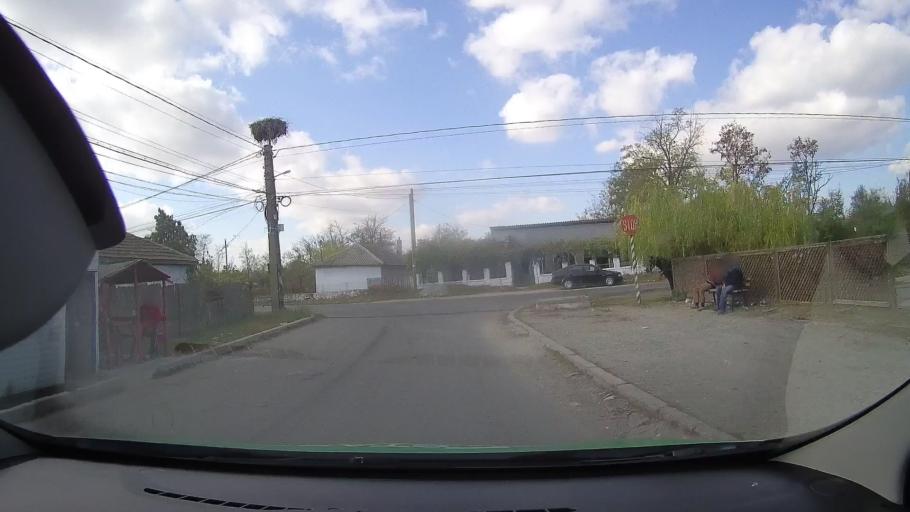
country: RO
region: Constanta
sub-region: Comuna Istria
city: Istria
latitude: 44.5727
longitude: 28.7083
